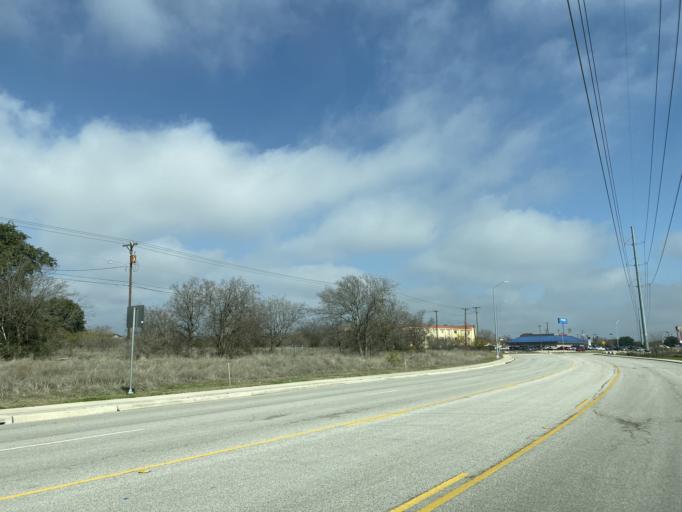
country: US
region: Texas
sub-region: Williamson County
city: Round Rock
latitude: 30.5274
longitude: -97.6935
